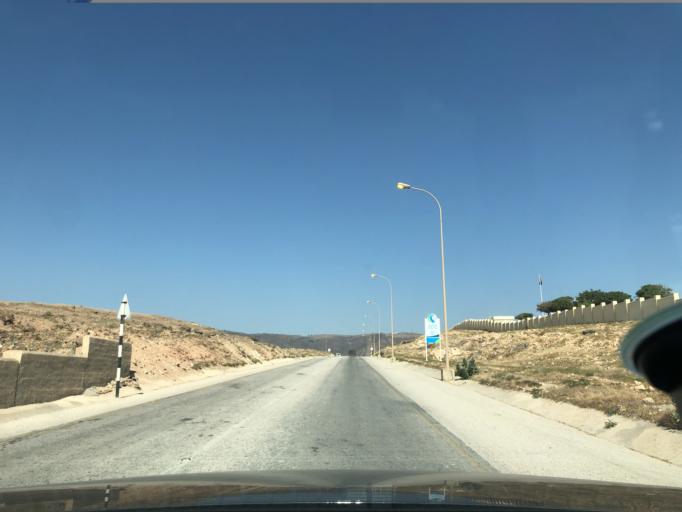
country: OM
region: Zufar
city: Salalah
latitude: 17.0402
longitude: 54.3988
